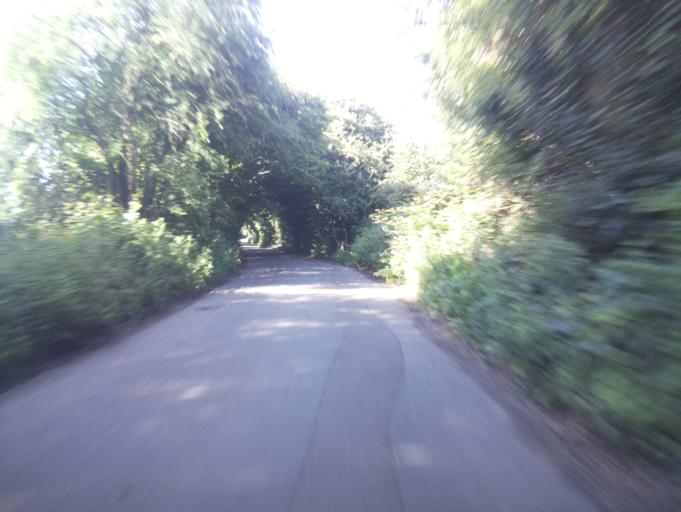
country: GB
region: England
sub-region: South Gloucestershire
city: Bitton
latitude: 51.4269
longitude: -2.4555
